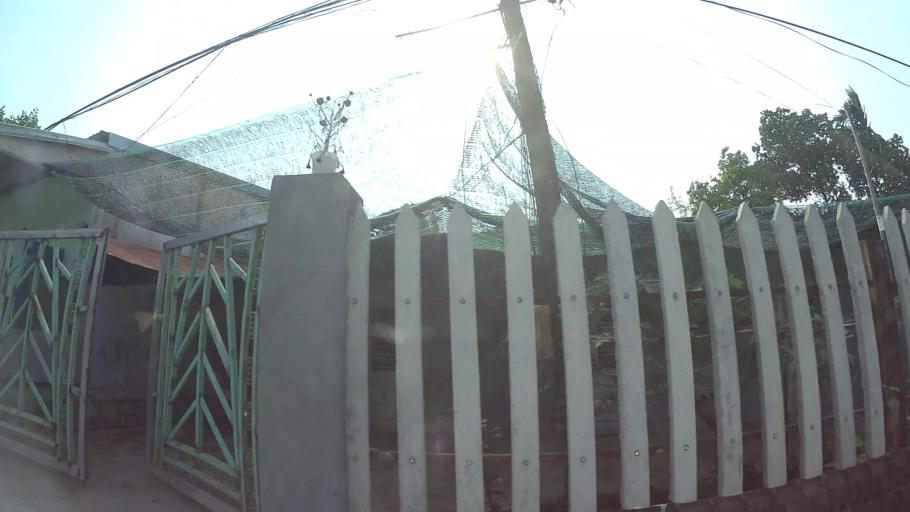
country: VN
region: Da Nang
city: Cam Le
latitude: 16.0144
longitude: 108.1851
